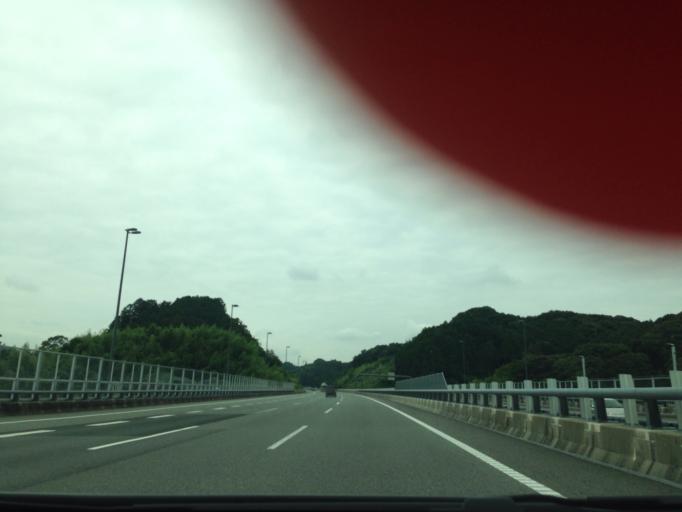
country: JP
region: Shizuoka
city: Mori
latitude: 34.8276
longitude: 137.8979
